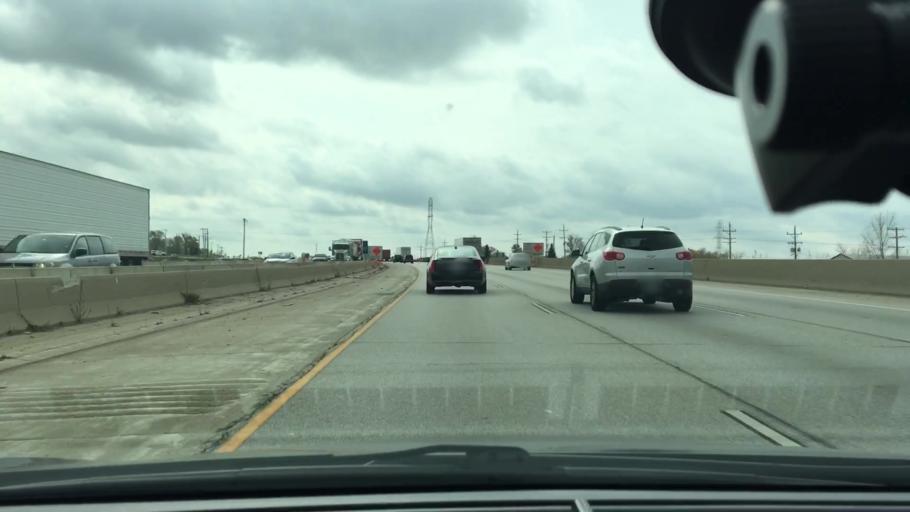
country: US
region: Wisconsin
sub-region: Racine County
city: Caledonia
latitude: 42.8418
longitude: -87.9520
